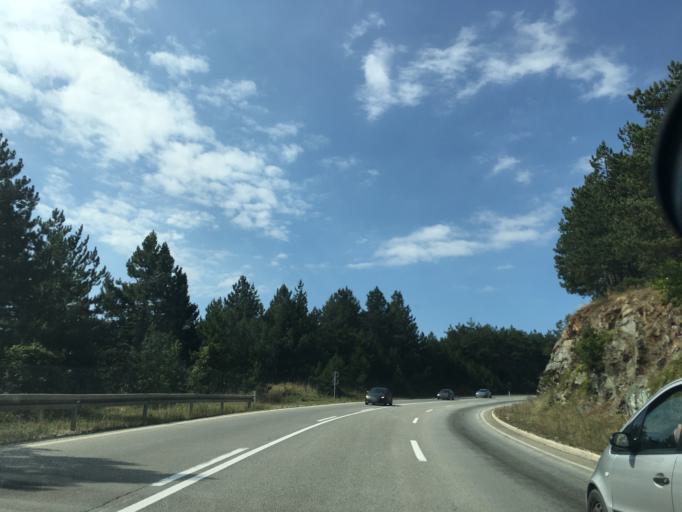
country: RS
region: Central Serbia
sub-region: Zlatiborski Okrug
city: Cajetina
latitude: 43.7555
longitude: 19.7212
